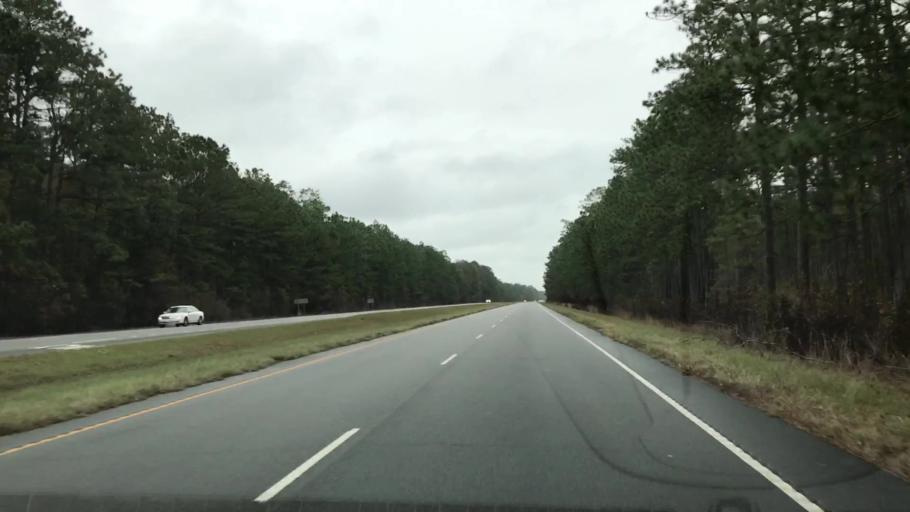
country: US
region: South Carolina
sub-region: Charleston County
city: Awendaw
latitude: 33.1301
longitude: -79.4466
